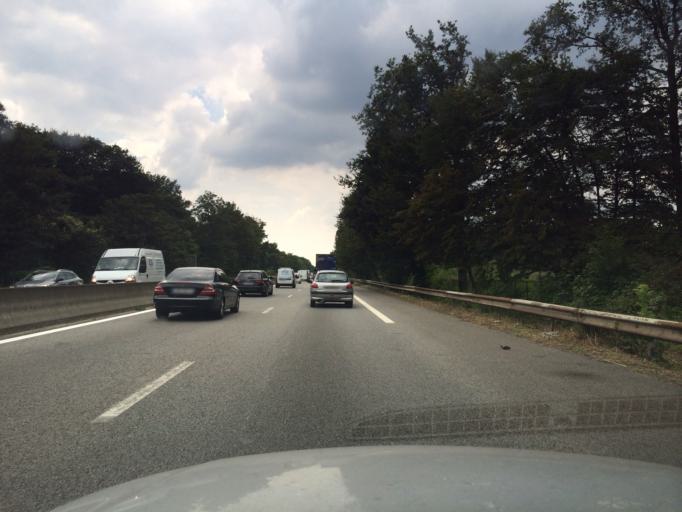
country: FR
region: Ile-de-France
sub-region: Departement des Yvelines
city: Noisy-le-Roi
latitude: 48.8512
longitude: 2.0668
